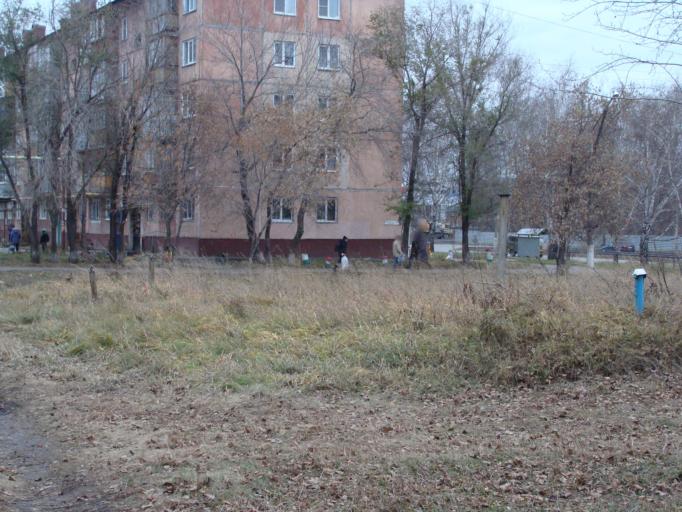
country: RU
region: Altai Krai
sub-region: Gorod Barnaulskiy
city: Barnaul
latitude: 53.3612
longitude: 83.6912
